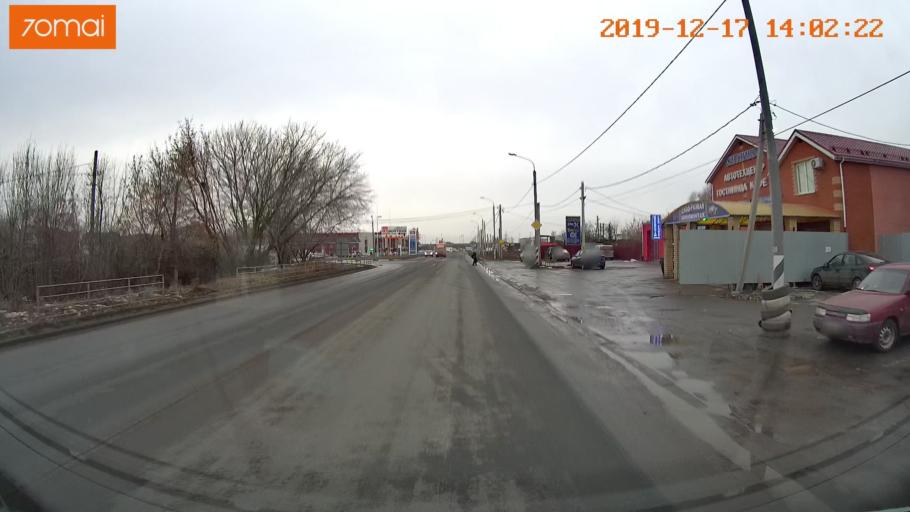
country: RU
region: Rjazan
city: Ryazan'
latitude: 54.6148
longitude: 39.6483
